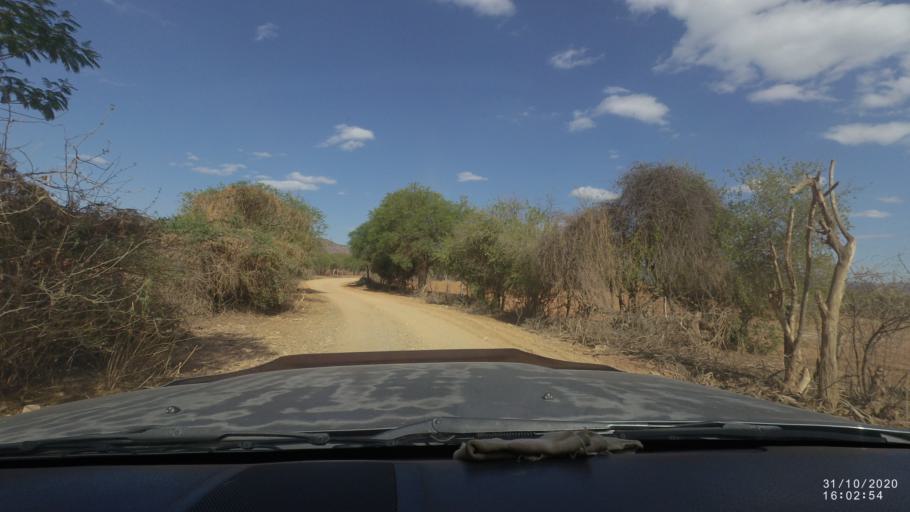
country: BO
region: Chuquisaca
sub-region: Provincia Zudanez
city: Mojocoya
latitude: -18.3492
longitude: -64.6553
